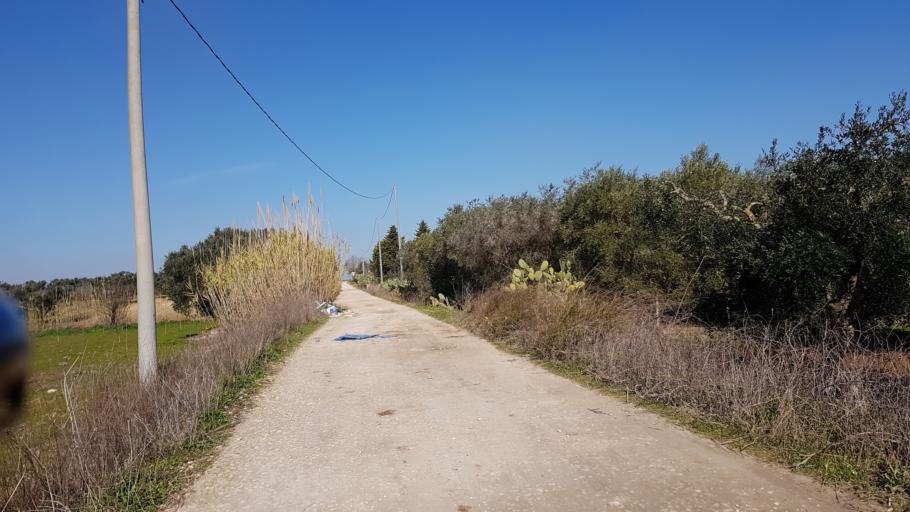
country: IT
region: Apulia
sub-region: Provincia di Brindisi
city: Mesagne
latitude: 40.6190
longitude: 17.8011
